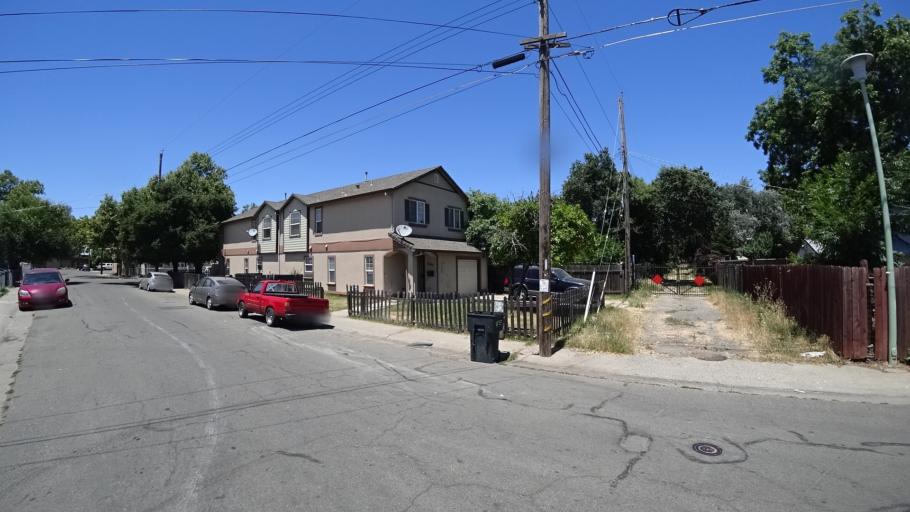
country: US
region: California
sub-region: Sacramento County
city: Parkway
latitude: 38.5376
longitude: -121.4718
